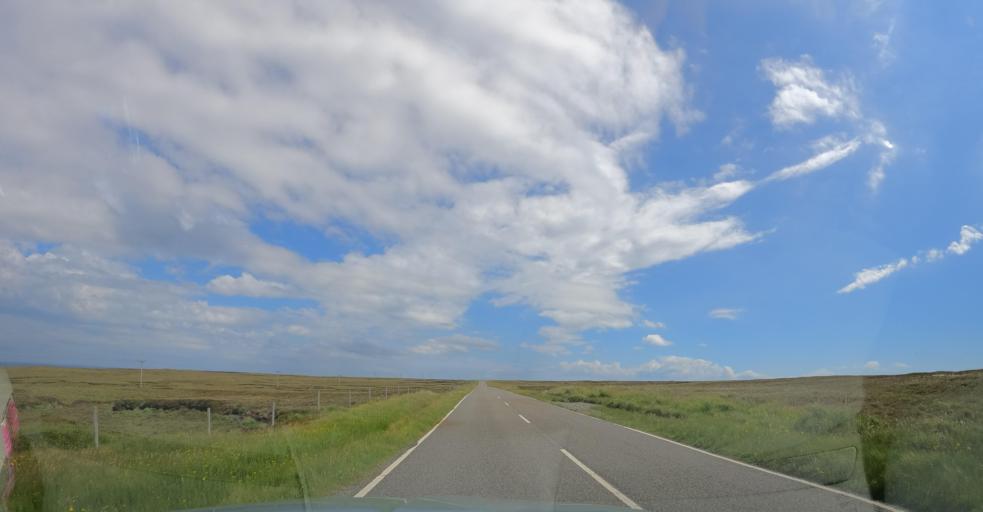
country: GB
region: Scotland
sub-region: Eilean Siar
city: Isle of Lewis
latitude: 58.4557
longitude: -6.3415
